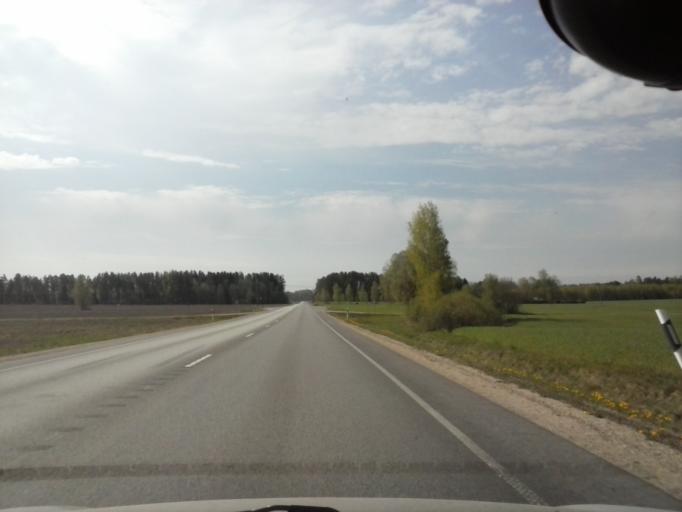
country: EE
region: Tartu
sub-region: UElenurme vald
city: Ulenurme
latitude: 58.2192
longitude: 26.7029
